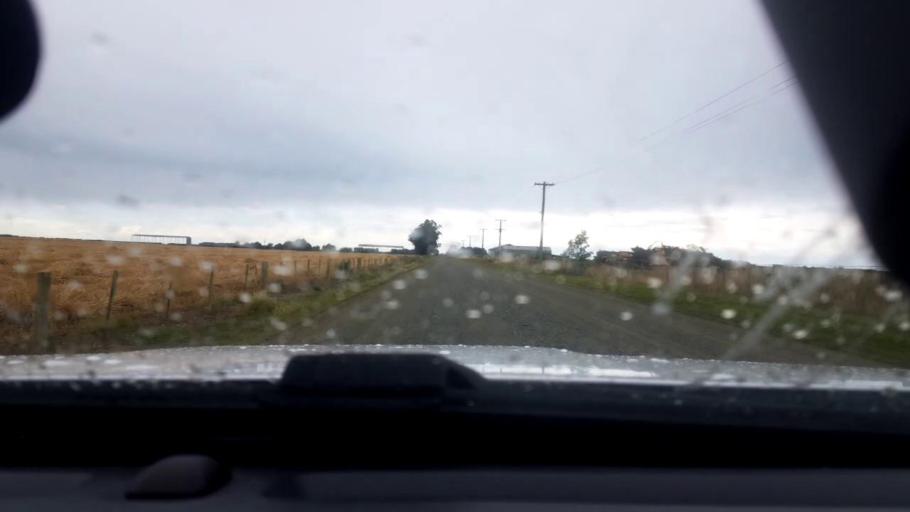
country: NZ
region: Canterbury
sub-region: Timaru District
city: Pleasant Point
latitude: -44.1336
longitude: 171.4078
